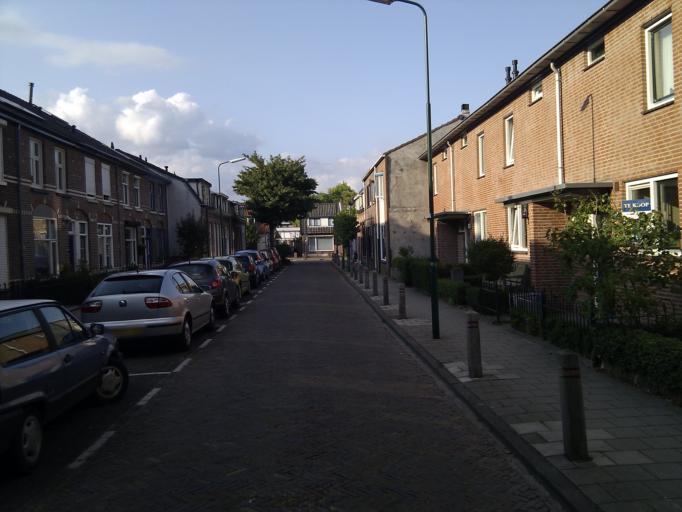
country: NL
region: Utrecht
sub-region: Gemeente De Bilt
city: De Bilt
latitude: 52.1082
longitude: 5.1824
